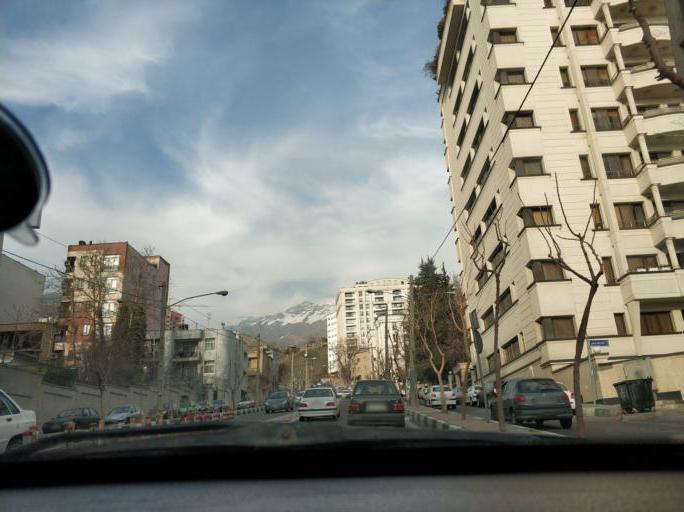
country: IR
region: Tehran
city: Tajrish
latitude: 35.8099
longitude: 51.4843
